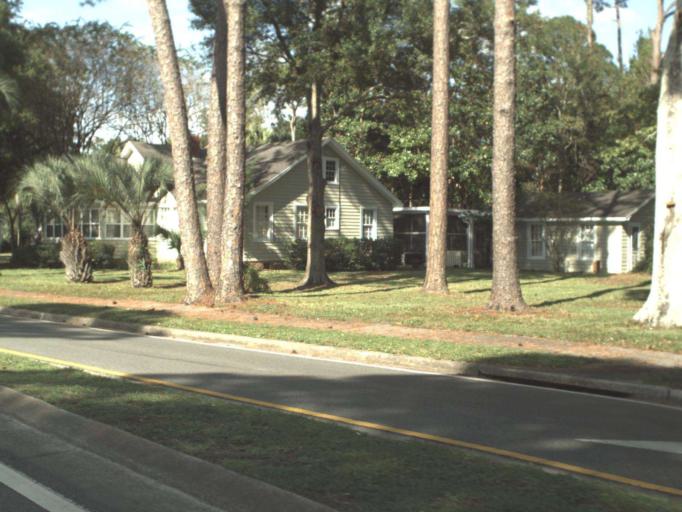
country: US
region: Florida
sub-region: Gulf County
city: Port Saint Joe
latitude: 29.8079
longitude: -85.3018
